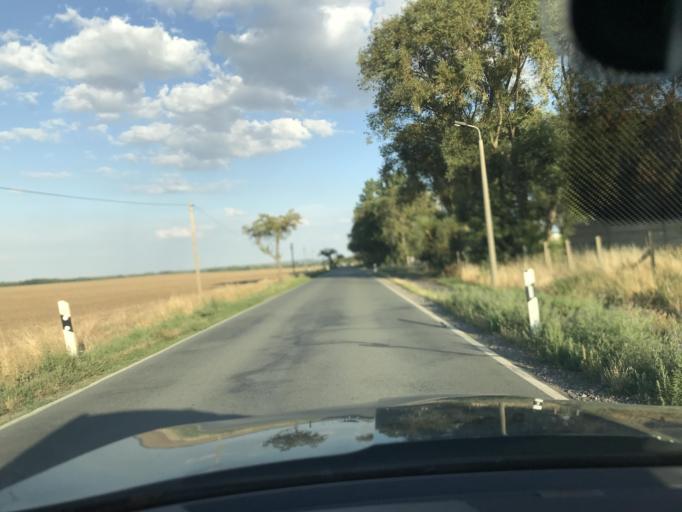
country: DE
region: Saxony-Anhalt
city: Schwanebeck
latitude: 51.9619
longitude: 11.1332
